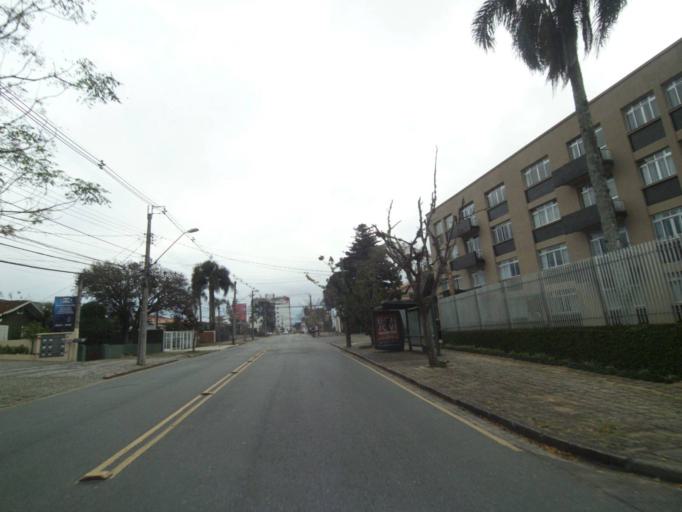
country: BR
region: Parana
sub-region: Curitiba
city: Curitiba
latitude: -25.3999
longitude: -49.2624
